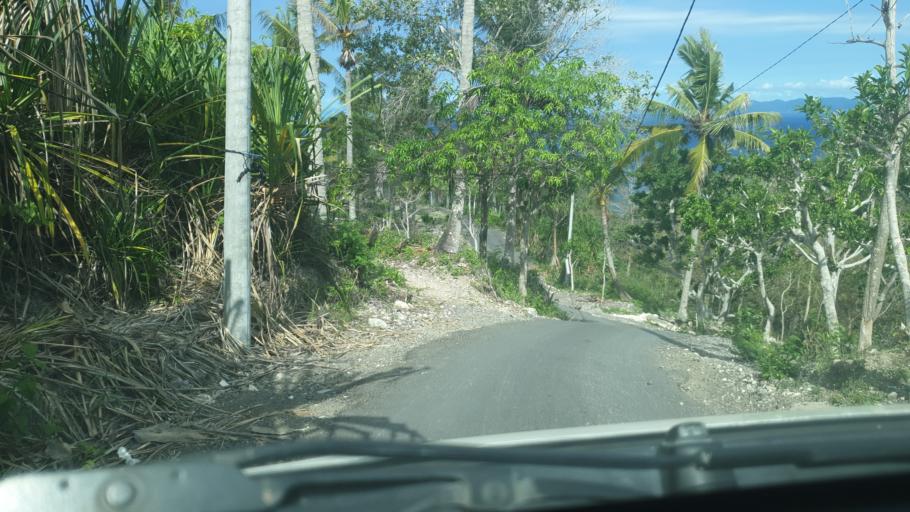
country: ID
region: Bali
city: Tanglad
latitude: -8.7751
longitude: 115.6159
